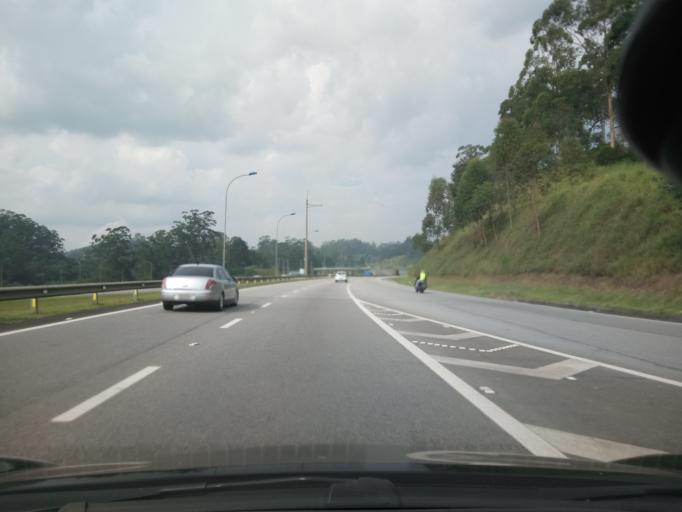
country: BR
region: Sao Paulo
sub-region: Sao Bernardo Do Campo
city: Sao Bernardo do Campo
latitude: -23.7647
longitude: -46.5866
